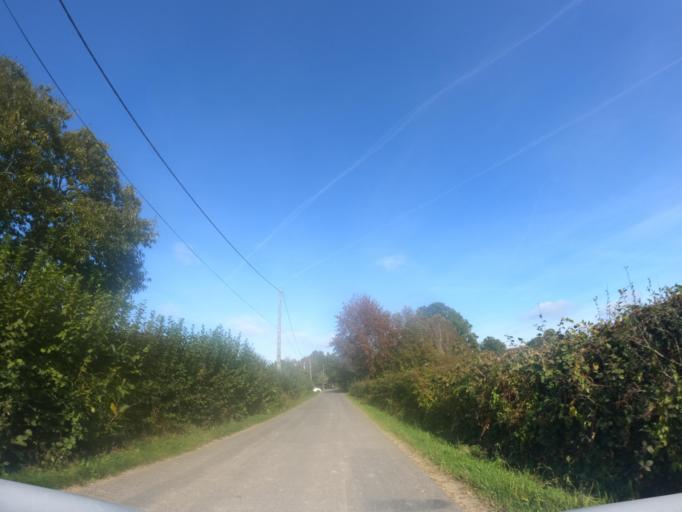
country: FR
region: Poitou-Charentes
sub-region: Departement des Deux-Sevres
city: Courlay
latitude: 46.7925
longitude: -0.5611
